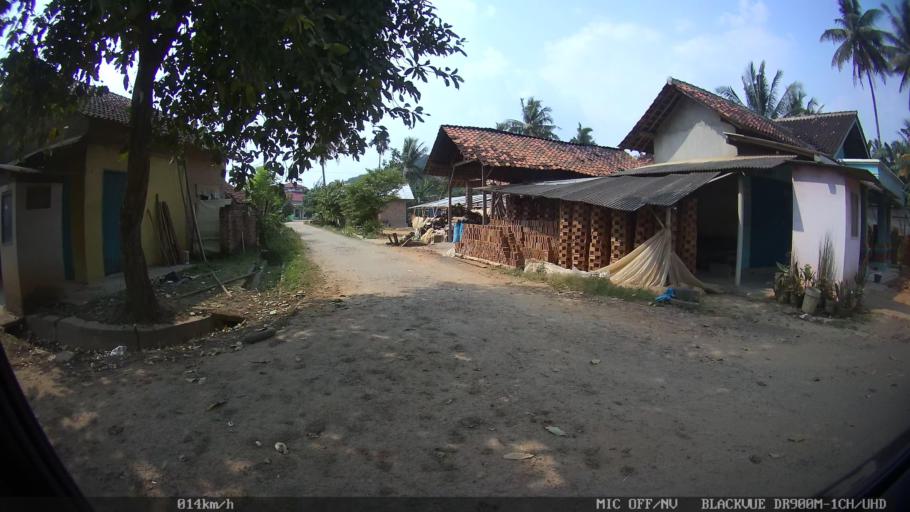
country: ID
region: Lampung
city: Pringsewu
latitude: -5.3820
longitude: 104.9980
